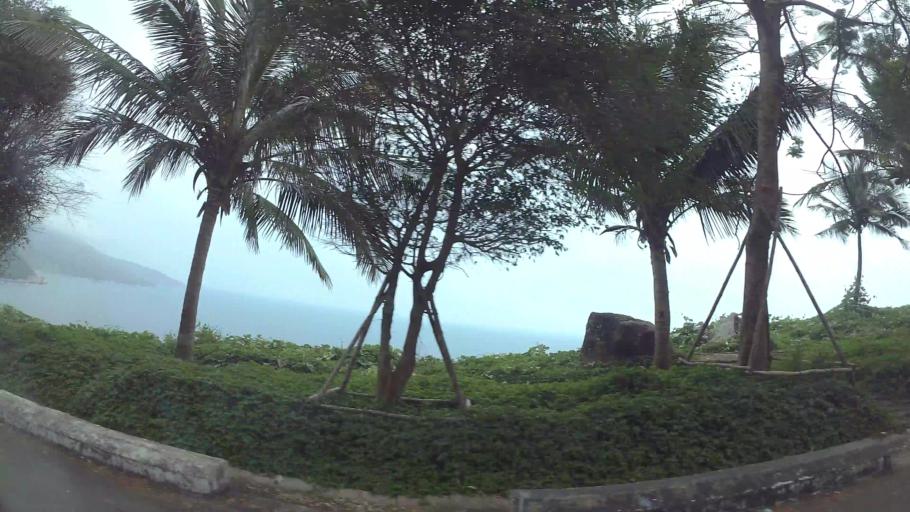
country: VN
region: Da Nang
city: Son Tra
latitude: 16.1056
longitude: 108.3078
